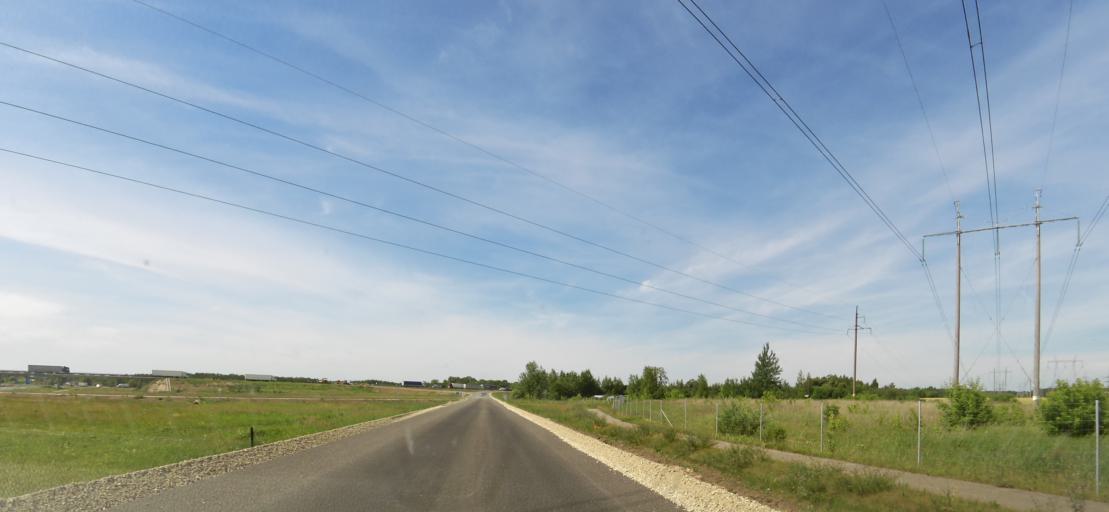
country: LT
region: Panevezys
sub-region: Panevezys City
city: Panevezys
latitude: 55.7334
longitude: 24.2814
